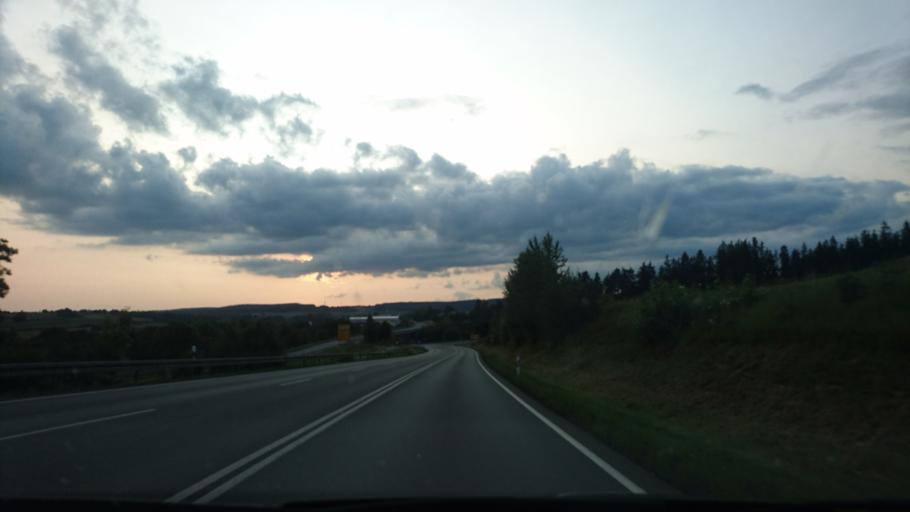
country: DE
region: Bavaria
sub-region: Upper Franconia
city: Selbitz
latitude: 50.3199
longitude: 11.7274
